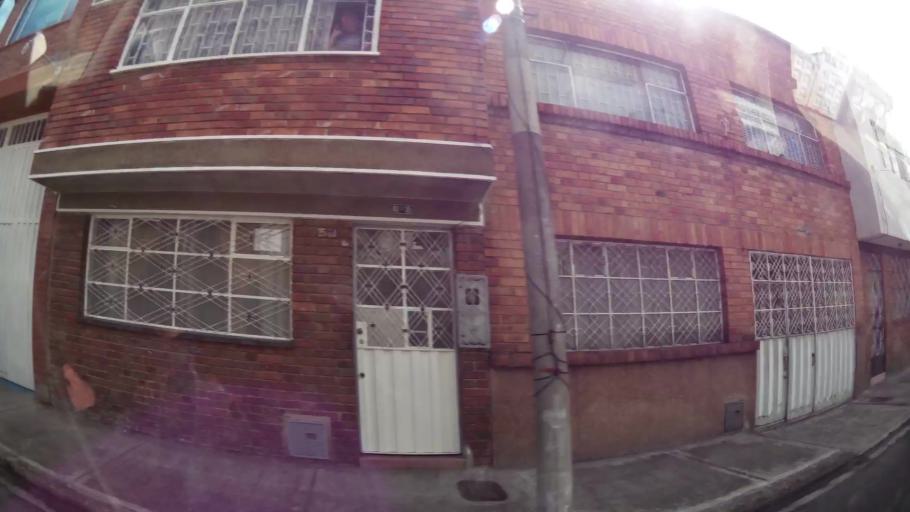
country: CO
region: Bogota D.C.
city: Barrio San Luis
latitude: 4.6774
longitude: -74.0648
